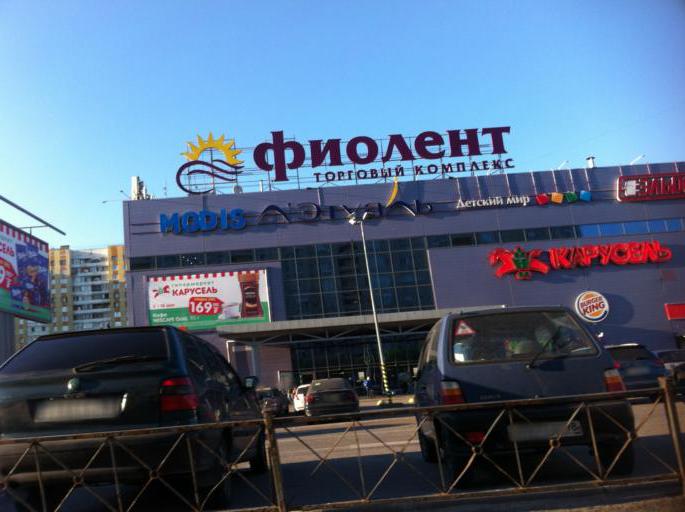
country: RU
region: St.-Petersburg
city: Dachnoye
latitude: 59.8525
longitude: 30.2186
